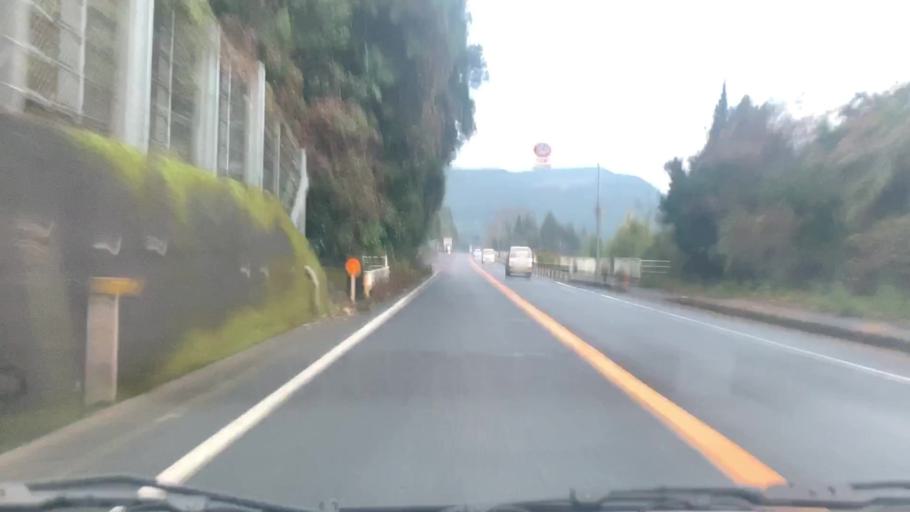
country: JP
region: Saga Prefecture
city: Ureshinomachi-shimojuku
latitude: 33.0776
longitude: 129.9660
